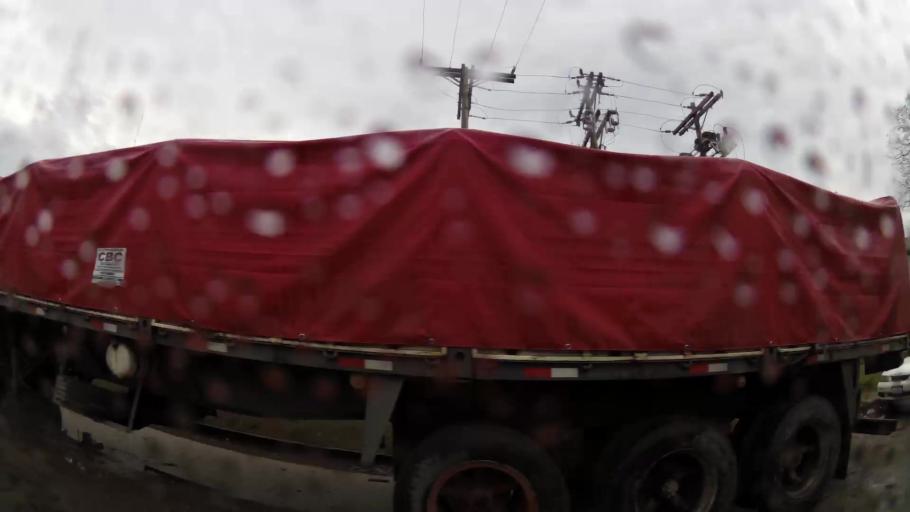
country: BO
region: Santa Cruz
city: Santa Cruz de la Sierra
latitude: -17.7741
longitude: -63.1421
